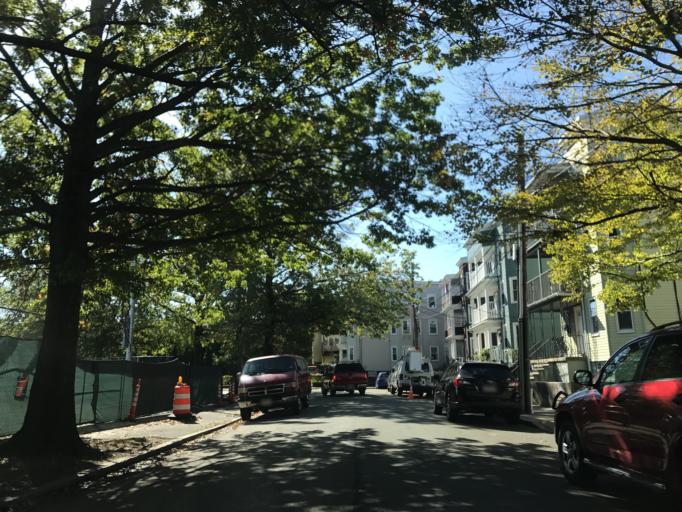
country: US
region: Massachusetts
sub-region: Middlesex County
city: Cambridge
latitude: 42.3783
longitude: -71.1015
